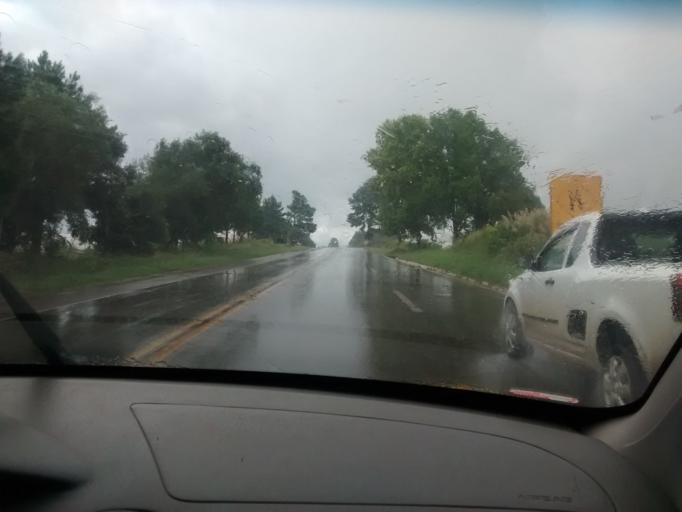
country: BR
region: Rio Grande do Sul
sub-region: Vacaria
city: Vacaria
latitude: -28.5464
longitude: -50.9751
